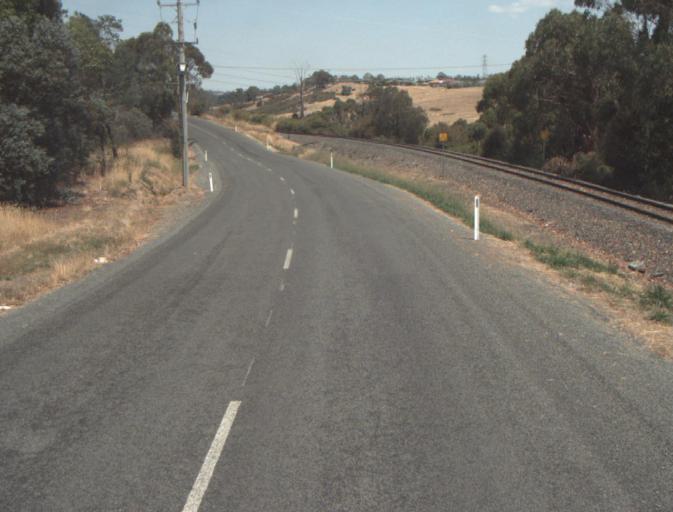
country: AU
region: Tasmania
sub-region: Launceston
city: Newstead
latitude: -41.4723
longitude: 147.1880
